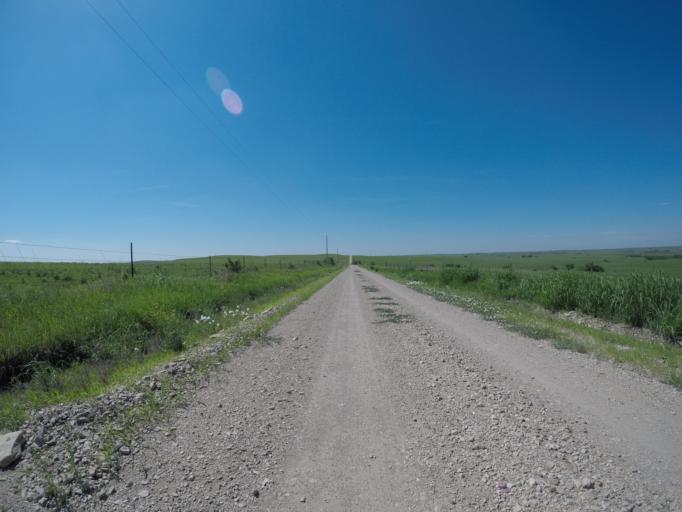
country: US
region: Kansas
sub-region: Wabaunsee County
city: Alma
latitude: 39.0086
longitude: -96.1783
